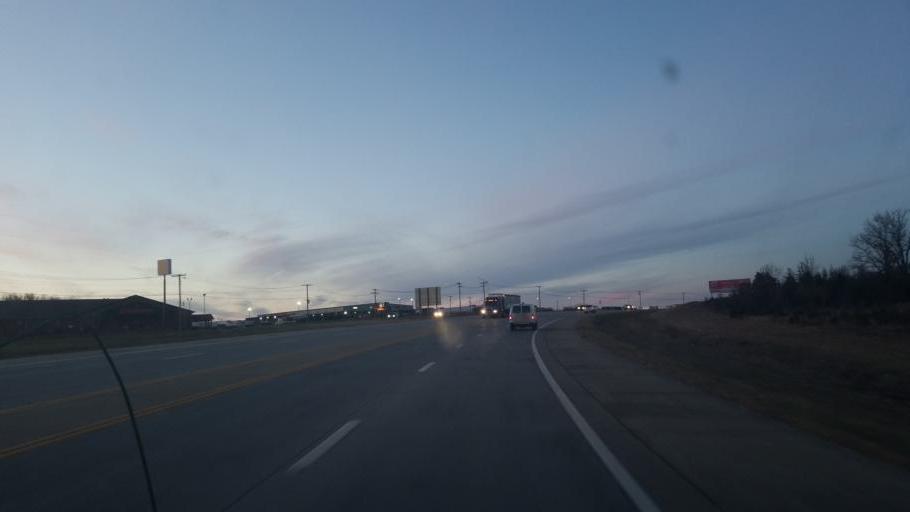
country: US
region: Missouri
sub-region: Howell County
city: West Plains
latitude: 36.7196
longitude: -91.8760
